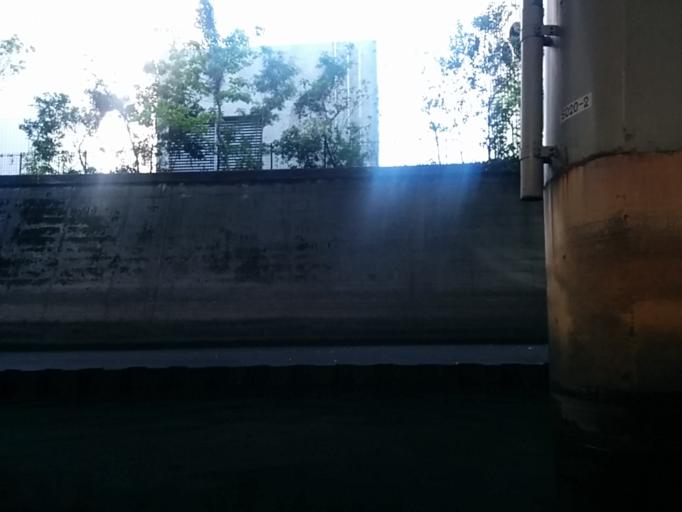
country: JP
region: Tokyo
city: Tokyo
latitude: 35.6940
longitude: 139.7543
